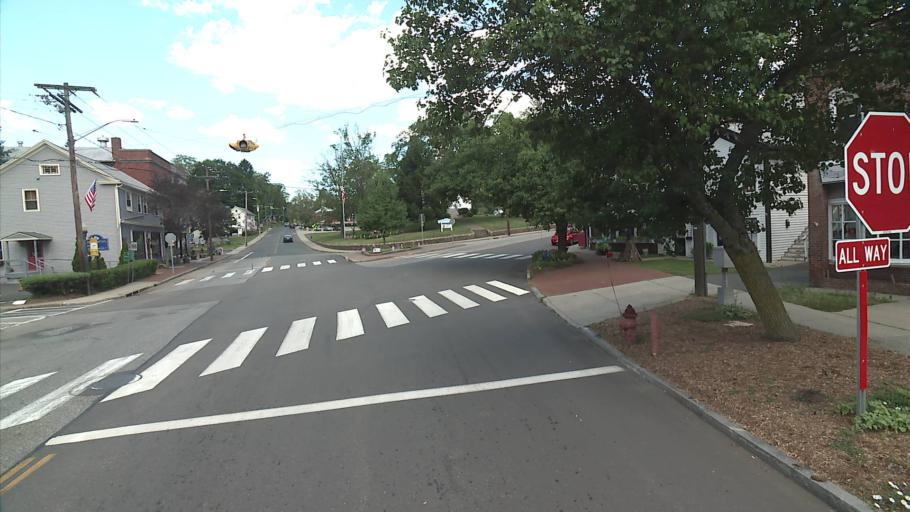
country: US
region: Connecticut
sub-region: Middlesex County
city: East Hampton
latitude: 41.5754
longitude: -72.5023
